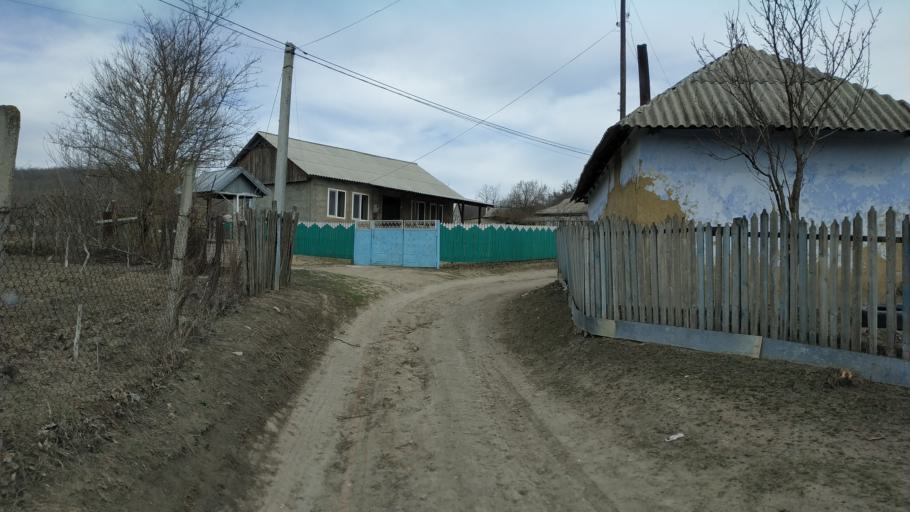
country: MD
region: Hincesti
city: Dancu
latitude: 46.9228
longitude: 28.2738
